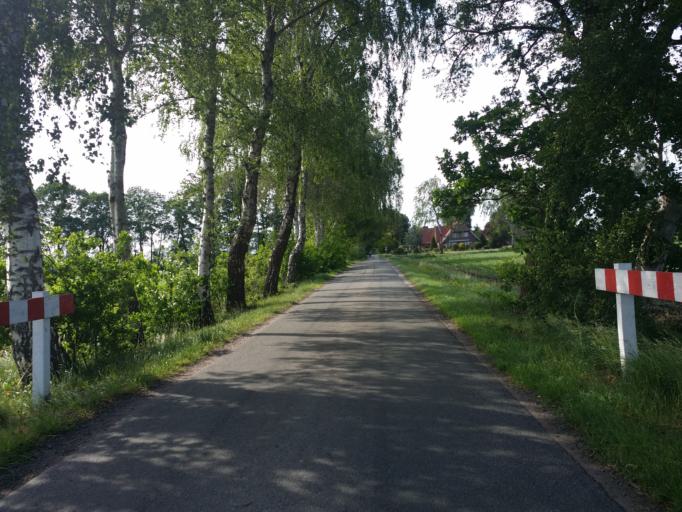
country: DE
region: Lower Saxony
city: Bockhorn
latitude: 53.3194
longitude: 8.0424
